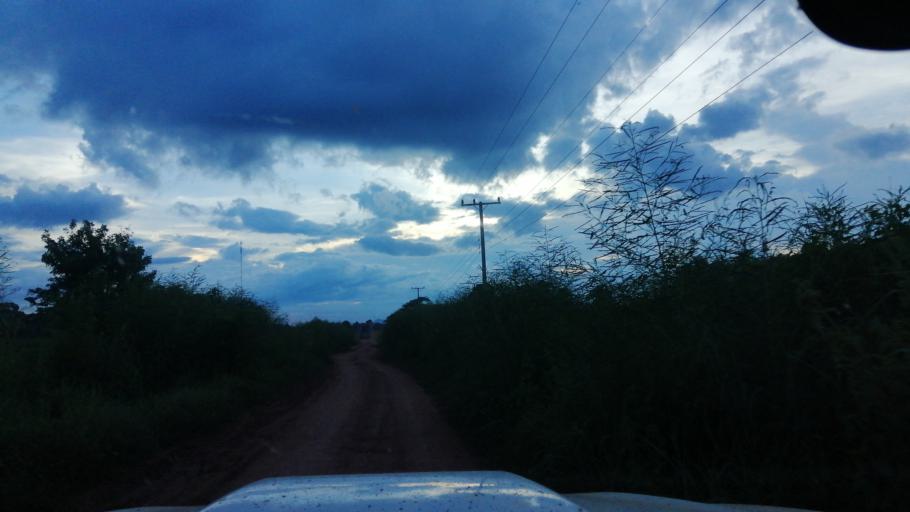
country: TH
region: Uttaradit
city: Ban Khok
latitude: 17.8784
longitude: 101.0581
